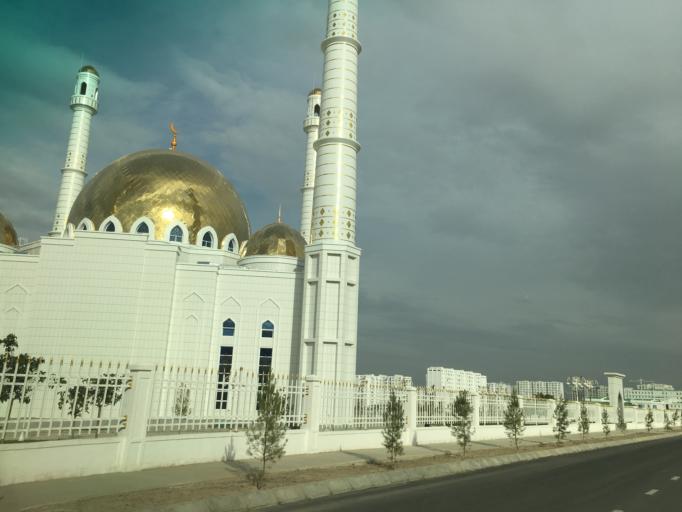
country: TM
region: Ahal
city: Ashgabat
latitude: 37.8972
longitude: 58.4117
